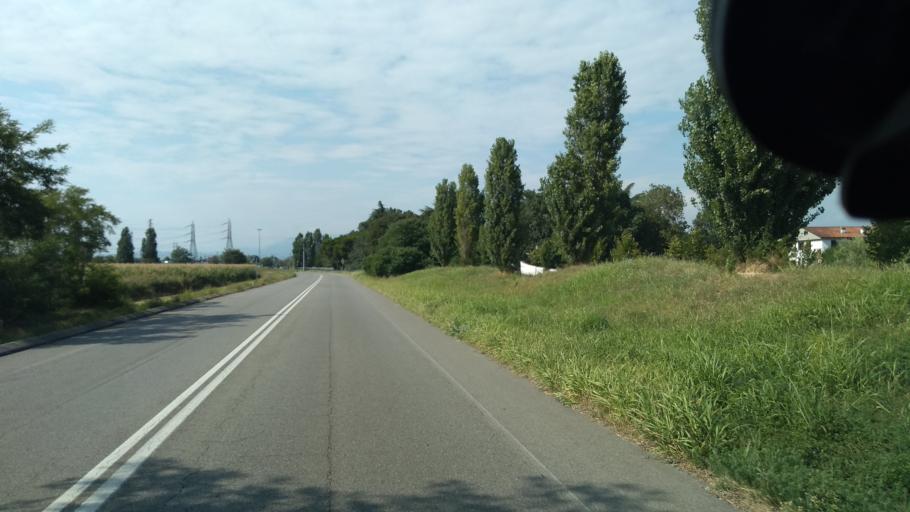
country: IT
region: Lombardy
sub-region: Provincia di Bergamo
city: Arcene
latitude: 45.5718
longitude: 9.6074
